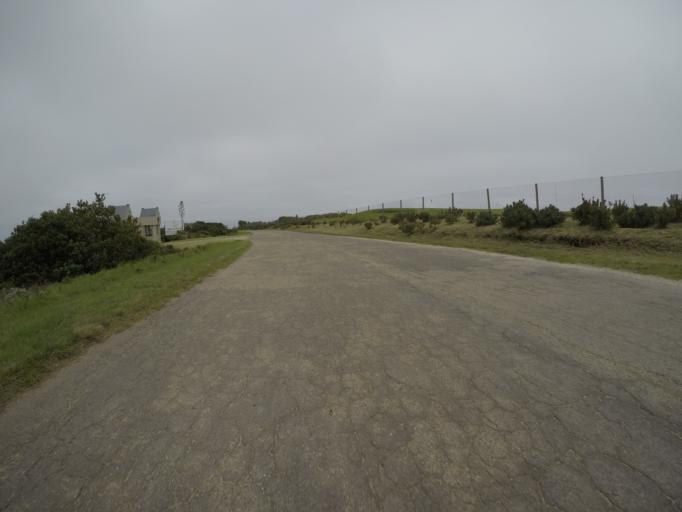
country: ZA
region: Eastern Cape
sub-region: Cacadu District Municipality
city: Kareedouw
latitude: -34.0724
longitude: 24.2325
